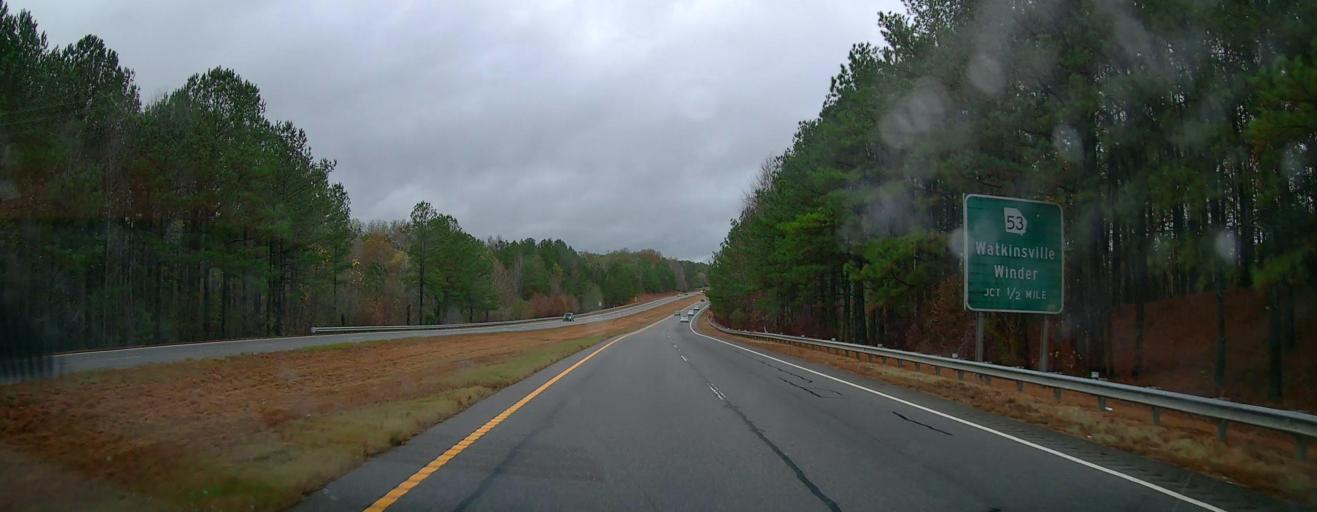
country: US
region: Georgia
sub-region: Oconee County
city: Watkinsville
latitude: 33.8589
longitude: -83.4247
